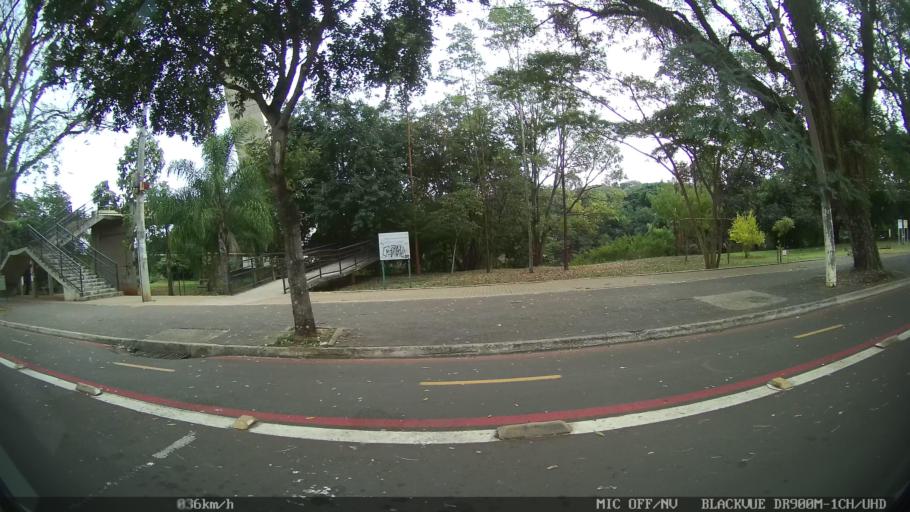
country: BR
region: Sao Paulo
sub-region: Piracicaba
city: Piracicaba
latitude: -22.7230
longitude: -47.6561
